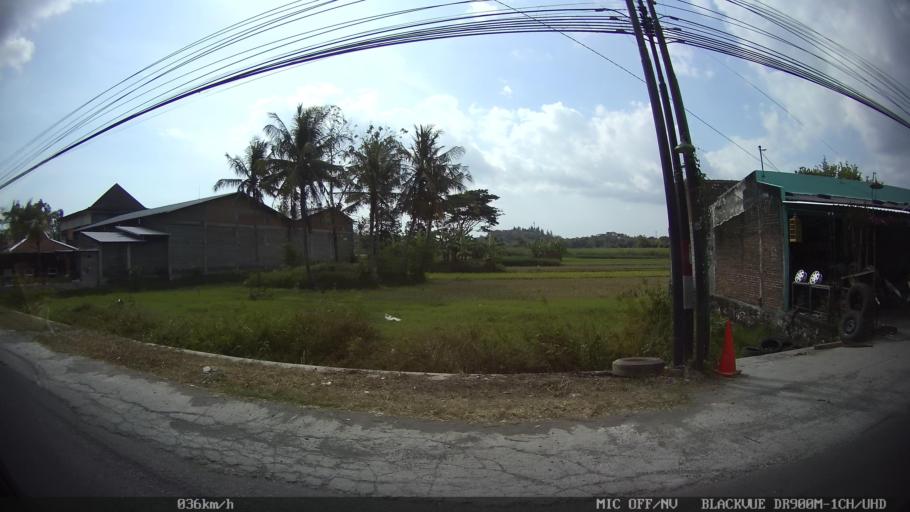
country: ID
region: Daerah Istimewa Yogyakarta
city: Kasihan
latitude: -7.8297
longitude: 110.3188
